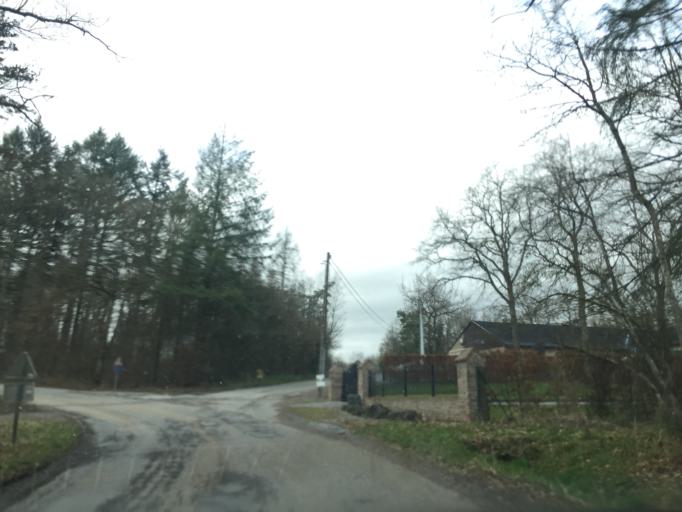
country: BE
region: Wallonia
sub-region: Province du Luxembourg
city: Durbuy
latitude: 50.3228
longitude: 5.4874
